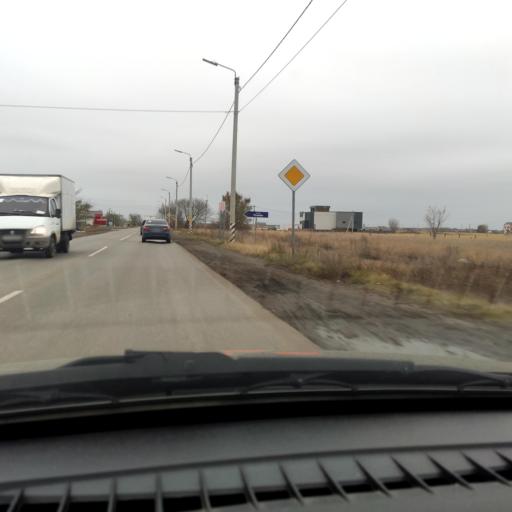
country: RU
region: Samara
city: Podstepki
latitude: 53.5220
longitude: 49.1820
